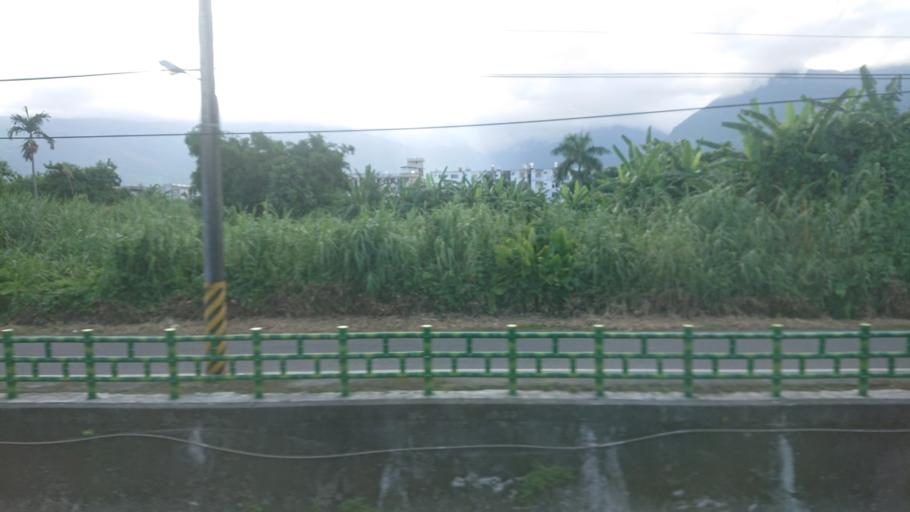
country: TW
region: Taiwan
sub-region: Hualien
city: Hualian
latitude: 23.9814
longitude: 121.5953
